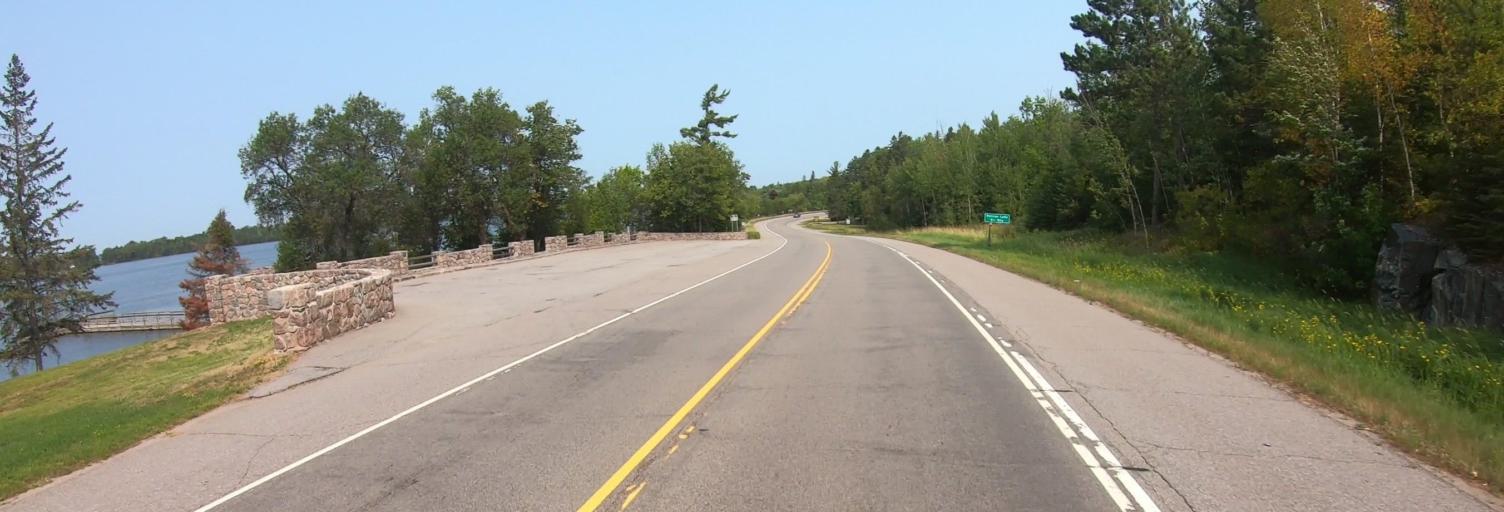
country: US
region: Minnesota
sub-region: Saint Louis County
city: Mountain Iron
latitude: 48.0587
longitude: -92.8304
